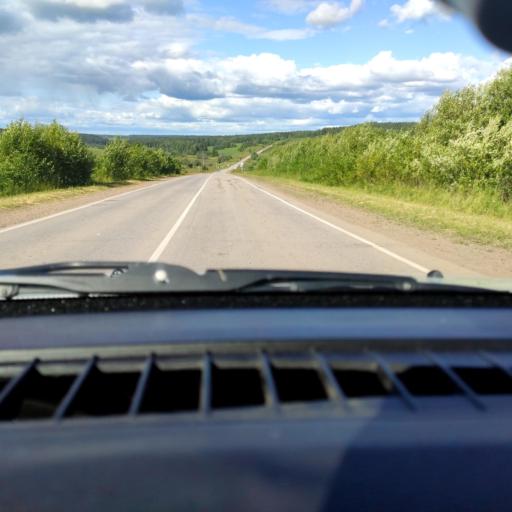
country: RU
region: Perm
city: Kukushtan
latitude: 57.3203
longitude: 56.5701
